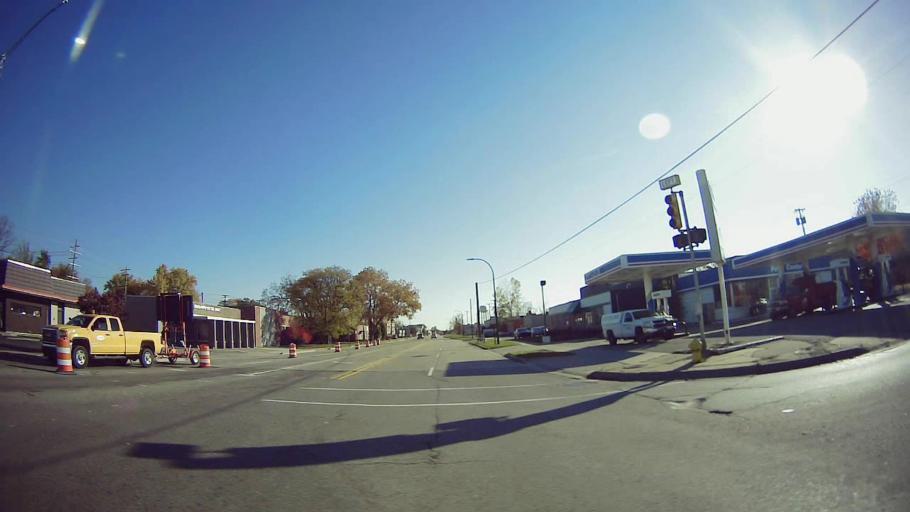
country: US
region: Michigan
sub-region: Oakland County
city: Lathrup Village
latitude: 42.4883
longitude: -83.2023
